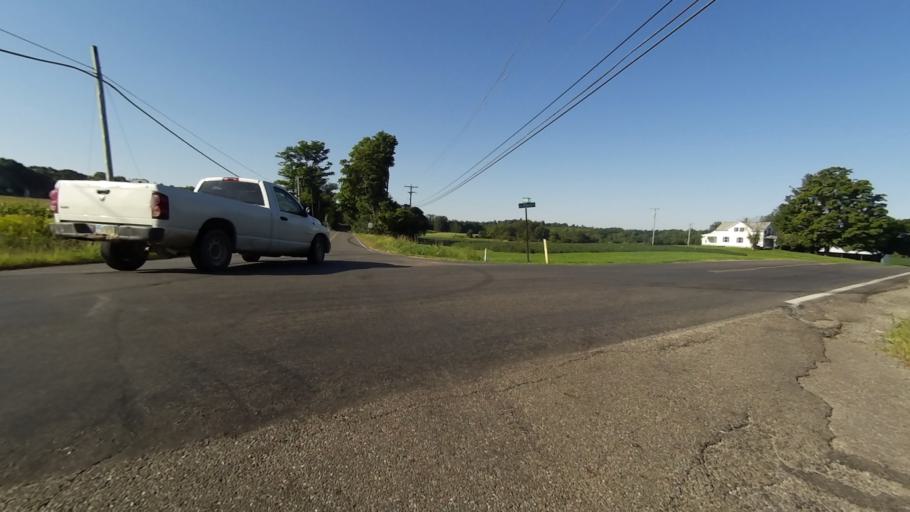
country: US
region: Ohio
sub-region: Portage County
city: Mantua
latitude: 41.2841
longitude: -81.2685
